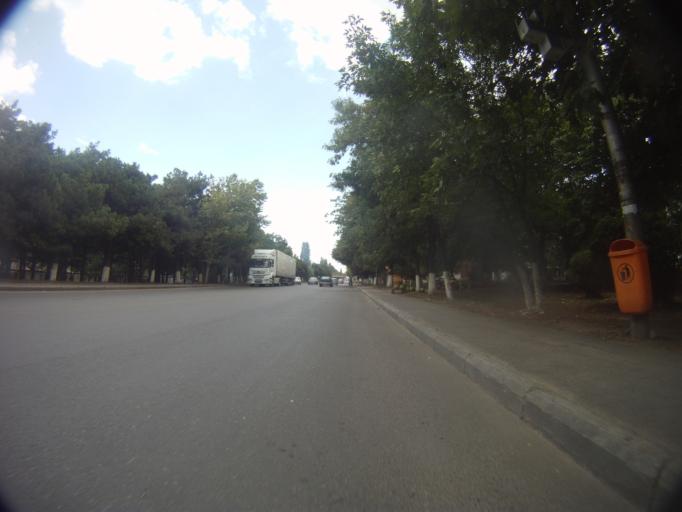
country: GE
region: T'bilisi
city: Tbilisi
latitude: 41.6452
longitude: 44.9113
